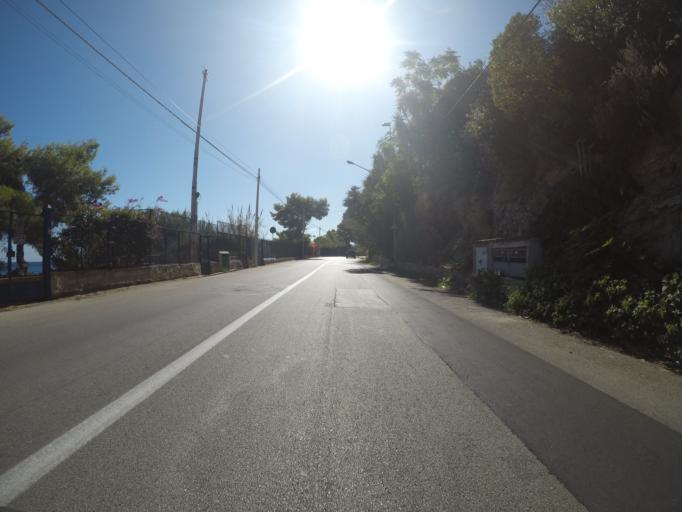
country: IT
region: Sicily
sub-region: Palermo
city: Palermo
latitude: 38.1837
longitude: 13.3638
